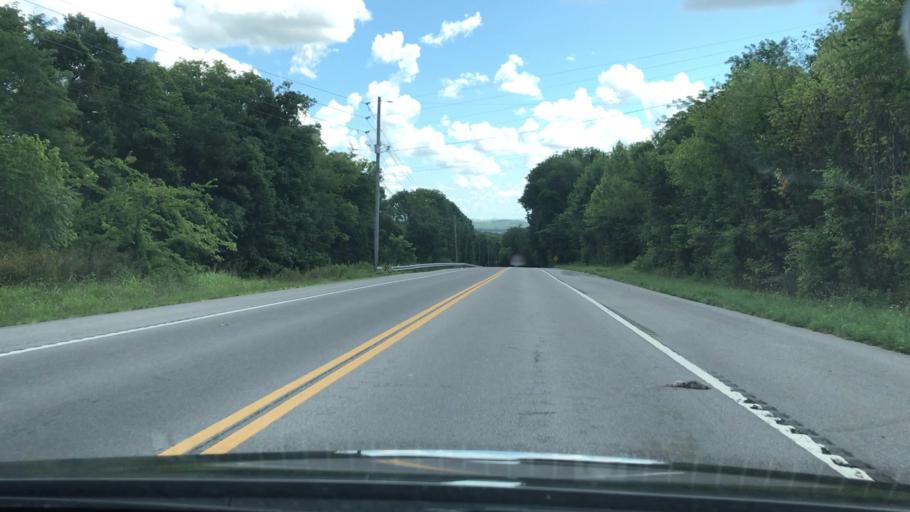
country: US
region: Tennessee
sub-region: Williamson County
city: Nolensville
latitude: 35.8503
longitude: -86.6077
